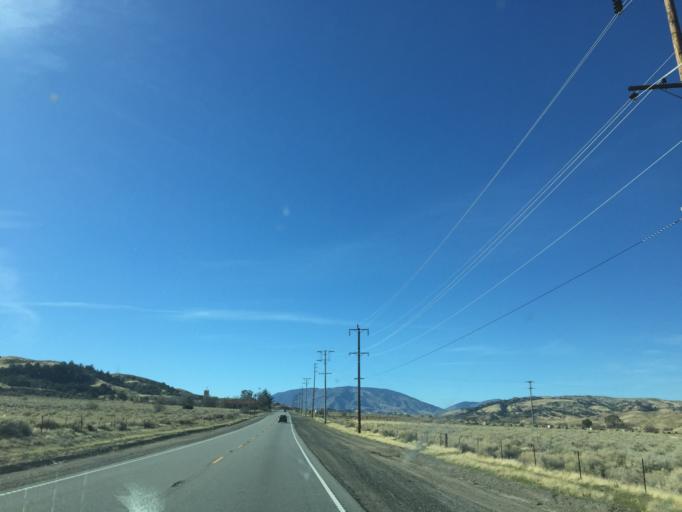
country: US
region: California
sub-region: Kern County
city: Lebec
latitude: 34.7649
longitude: -118.7194
